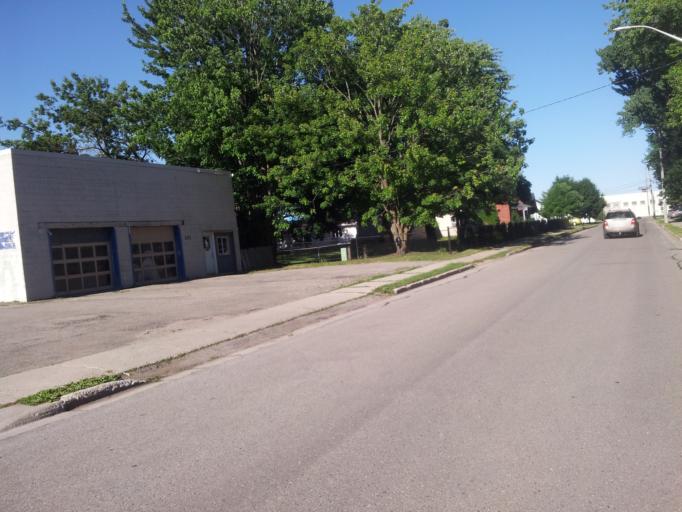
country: CA
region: Ontario
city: Stratford
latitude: 43.3702
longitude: -80.9597
